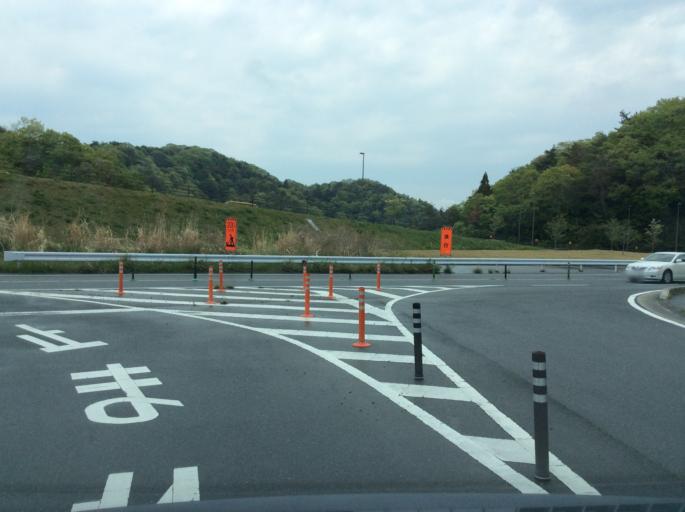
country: JP
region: Fukushima
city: Iwaki
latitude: 37.0386
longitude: 140.9283
